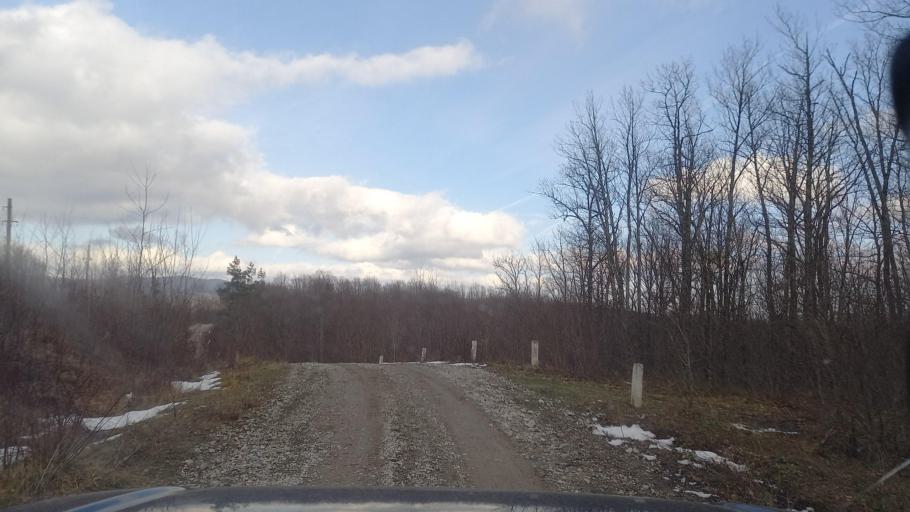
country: RU
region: Krasnodarskiy
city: Smolenskaya
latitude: 44.5738
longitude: 38.8005
